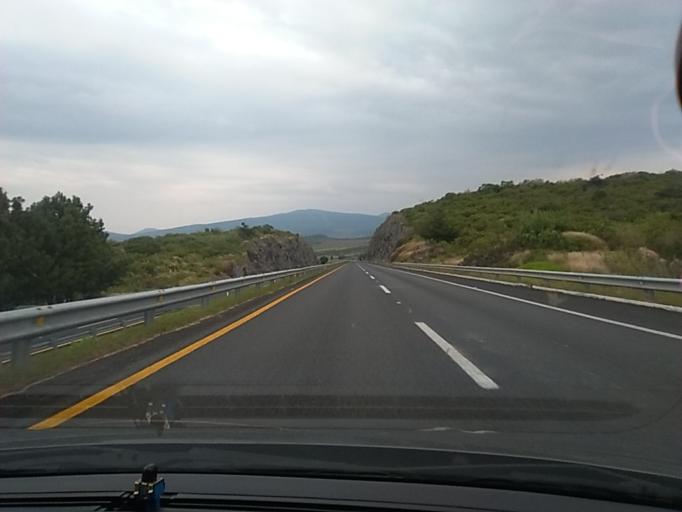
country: MX
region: Michoacan
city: Penjamillo de Degollado
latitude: 20.0644
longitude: -101.9644
